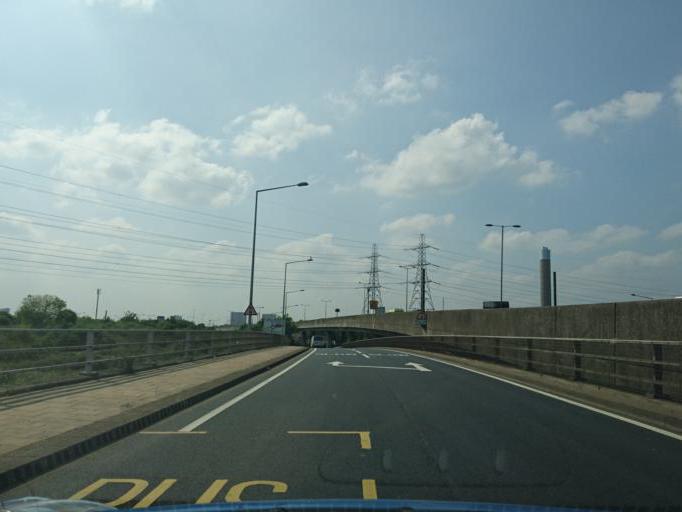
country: GB
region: England
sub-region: Greater London
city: Walthamstow
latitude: 51.6126
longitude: -0.0344
